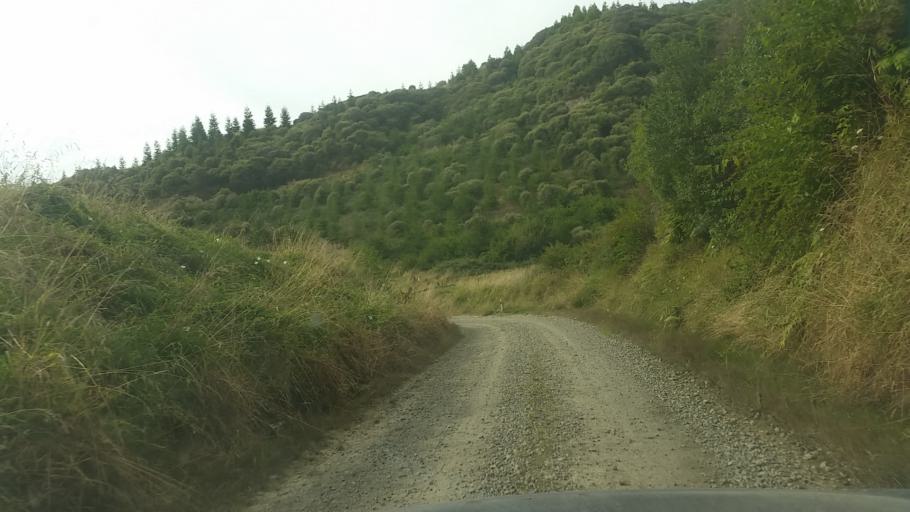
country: NZ
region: Taranaki
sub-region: New Plymouth District
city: Waitara
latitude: -39.1377
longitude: 174.7139
